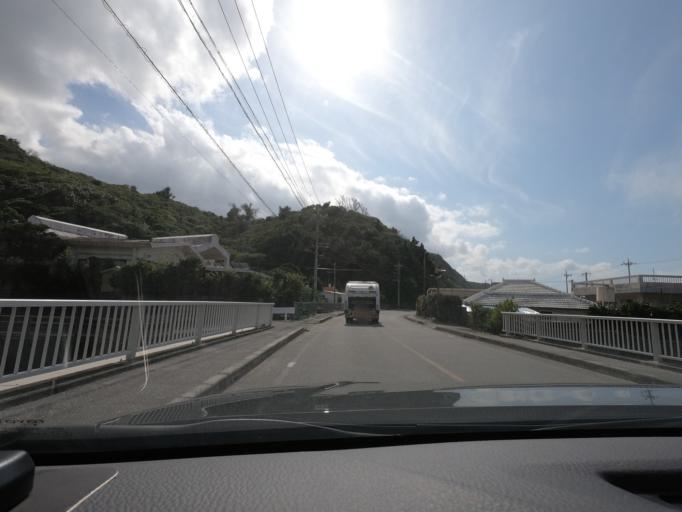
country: JP
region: Okinawa
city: Nago
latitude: 26.7563
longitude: 128.1891
